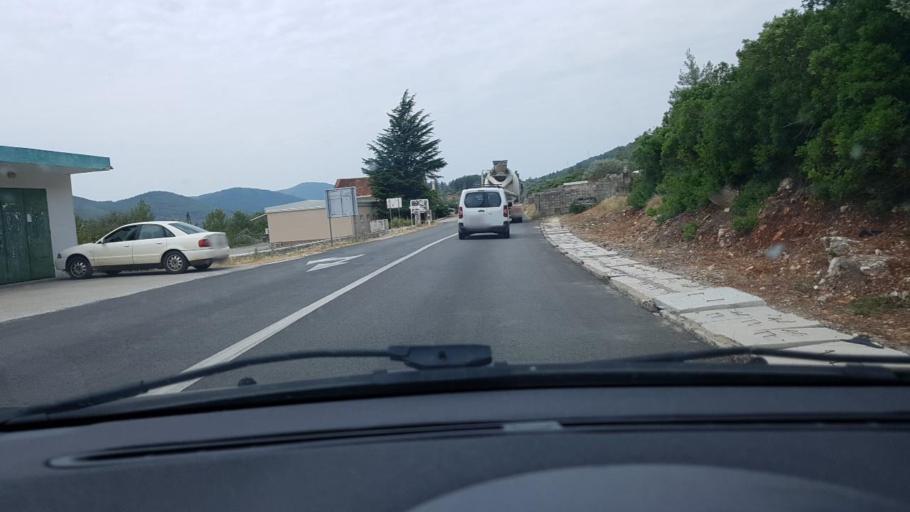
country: HR
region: Dubrovacko-Neretvanska
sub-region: Grad Dubrovnik
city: Vela Luka
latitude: 42.9473
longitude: 16.7756
